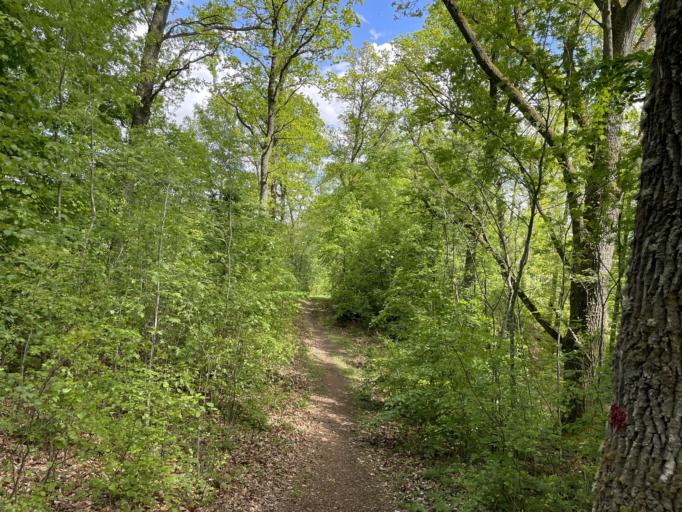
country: SE
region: Skane
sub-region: Klippans Kommun
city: Klippan
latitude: 56.1600
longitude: 13.1532
